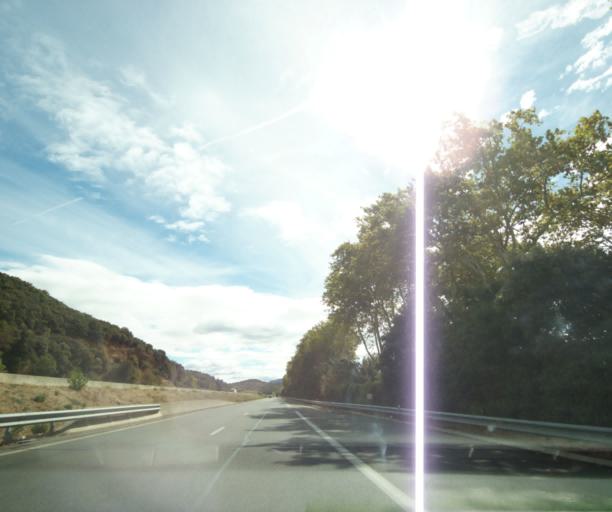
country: FR
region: Languedoc-Roussillon
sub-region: Departement de l'Herault
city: Lodeve
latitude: 43.7076
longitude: 3.3267
